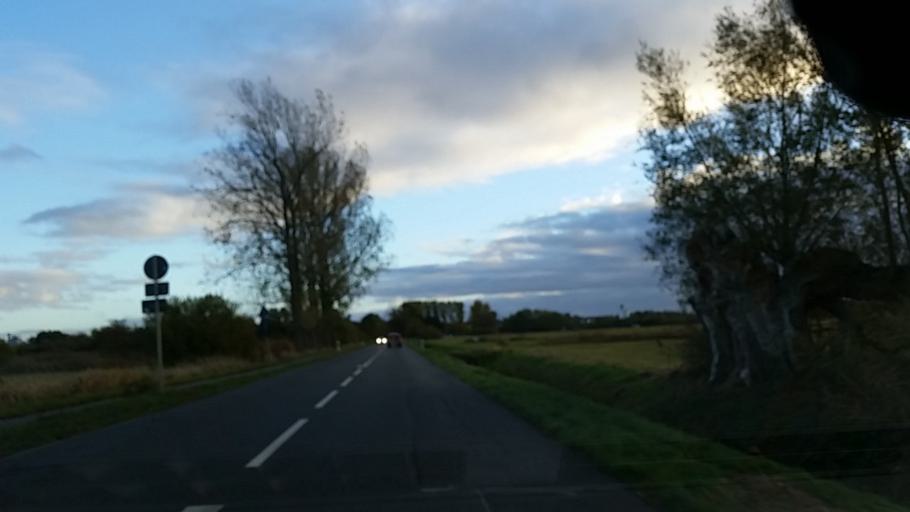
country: DE
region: Lower Saxony
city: Weyhausen
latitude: 52.4336
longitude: 10.7150
